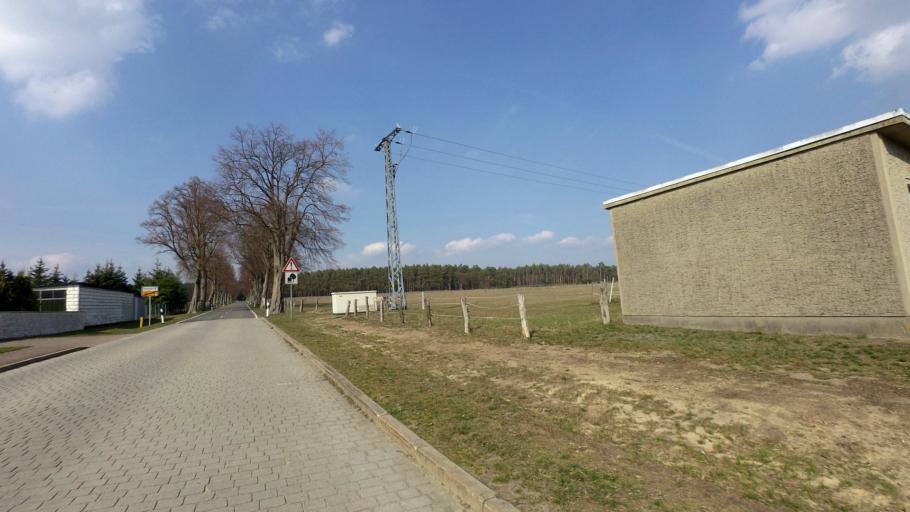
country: DE
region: Brandenburg
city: Dahme
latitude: 51.9421
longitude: 13.4427
